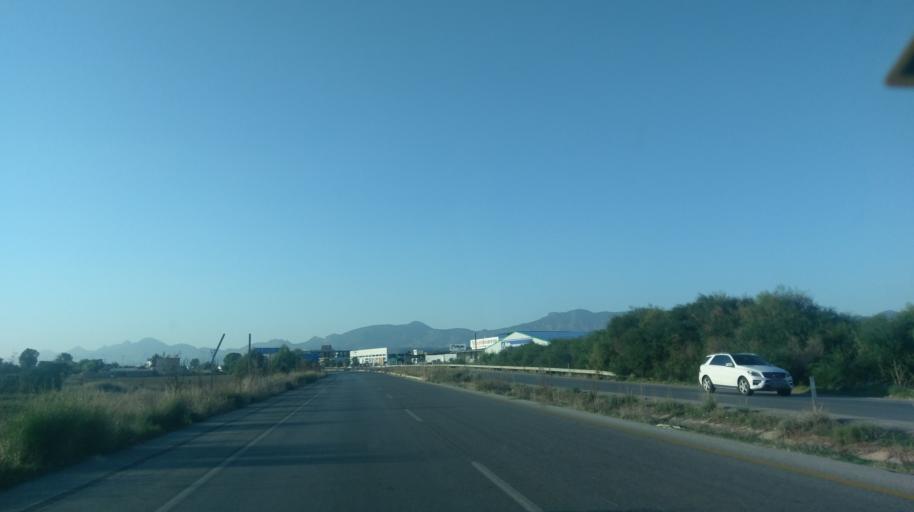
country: CY
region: Ammochostos
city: Lefkonoiko
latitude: 35.2055
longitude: 33.5968
